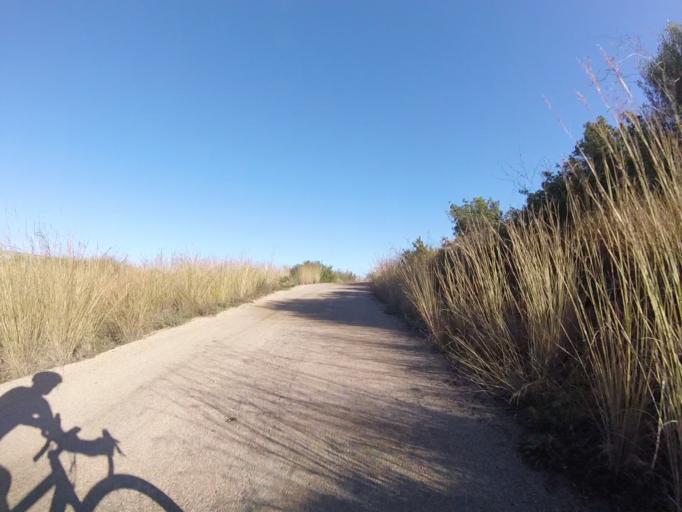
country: ES
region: Valencia
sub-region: Provincia de Castello
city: Santa Magdalena de Pulpis
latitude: 40.3480
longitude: 0.2926
